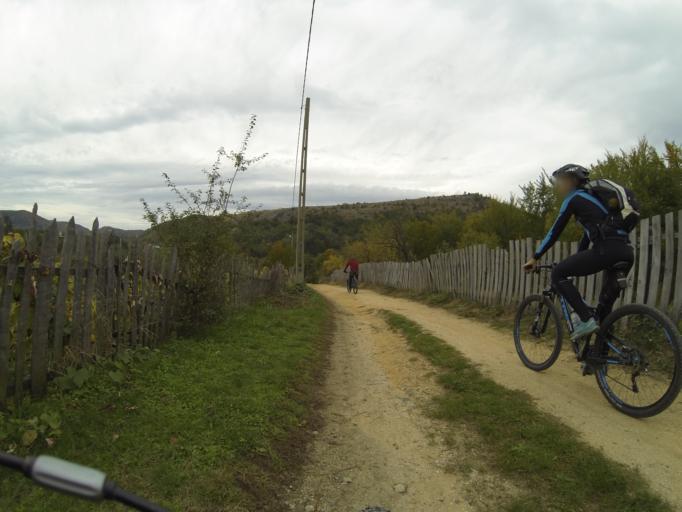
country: RO
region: Gorj
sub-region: Comuna Tismana
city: Sohodol
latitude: 45.0584
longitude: 22.8884
